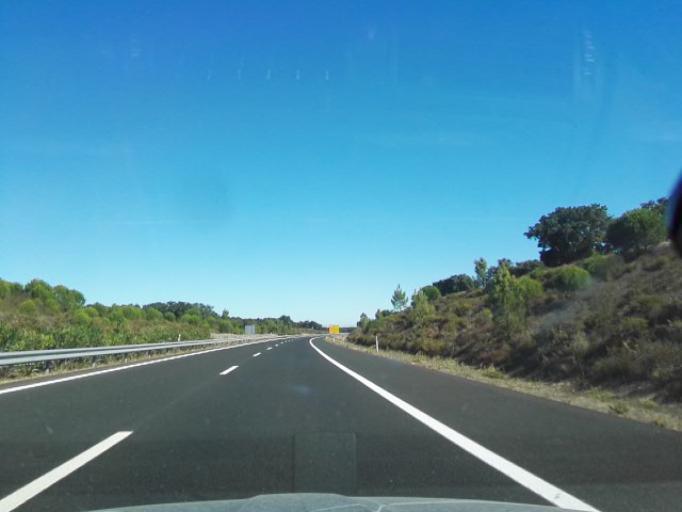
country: PT
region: Santarem
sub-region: Benavente
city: Poceirao
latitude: 38.8807
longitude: -8.7940
